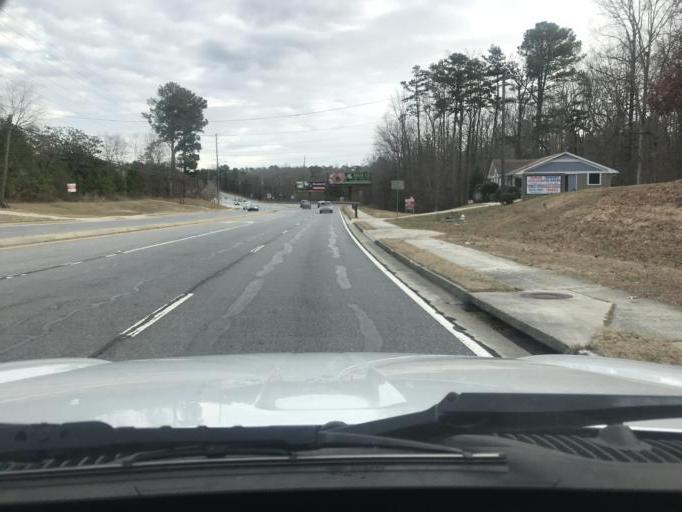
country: US
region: Georgia
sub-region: Gwinnett County
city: Buford
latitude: 34.0726
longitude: -83.9767
